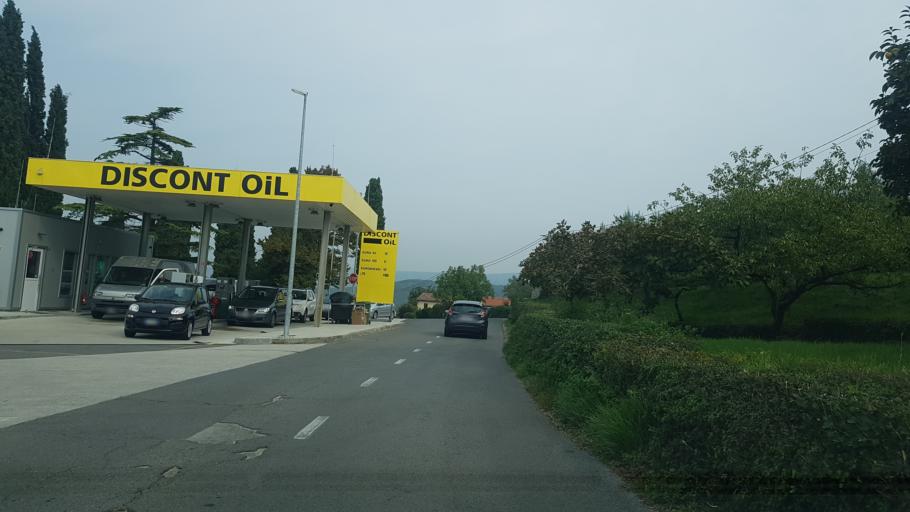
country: SI
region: Koper-Capodistria
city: Spodnje Skofije
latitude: 45.5759
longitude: 13.8032
